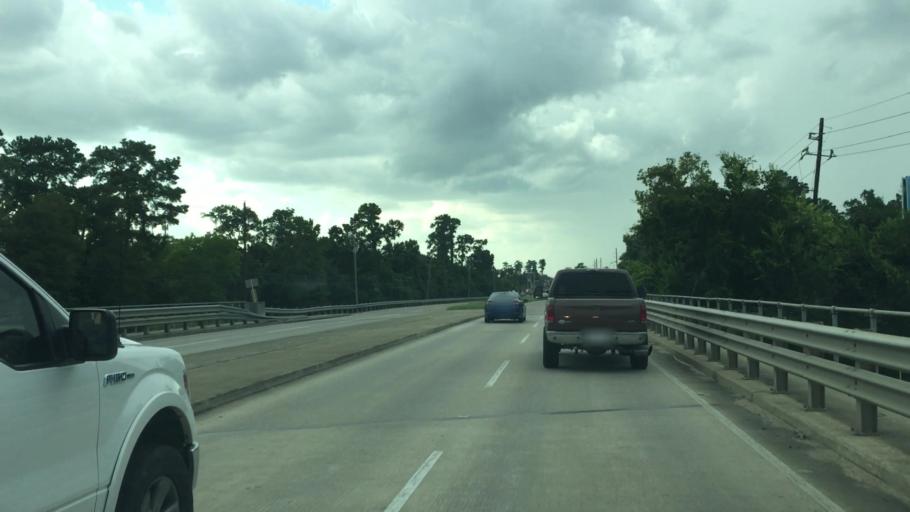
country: US
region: Texas
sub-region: Harris County
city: Hudson
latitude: 30.0068
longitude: -95.5121
